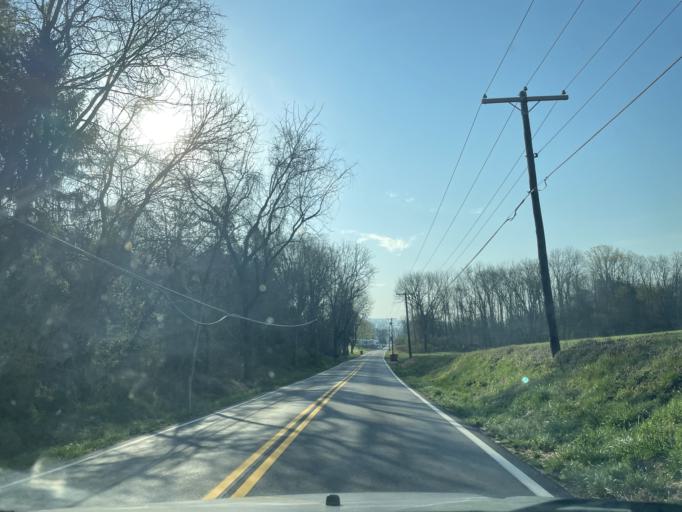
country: US
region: Maryland
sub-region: Washington County
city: Saint James
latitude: 39.5467
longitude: -77.7235
